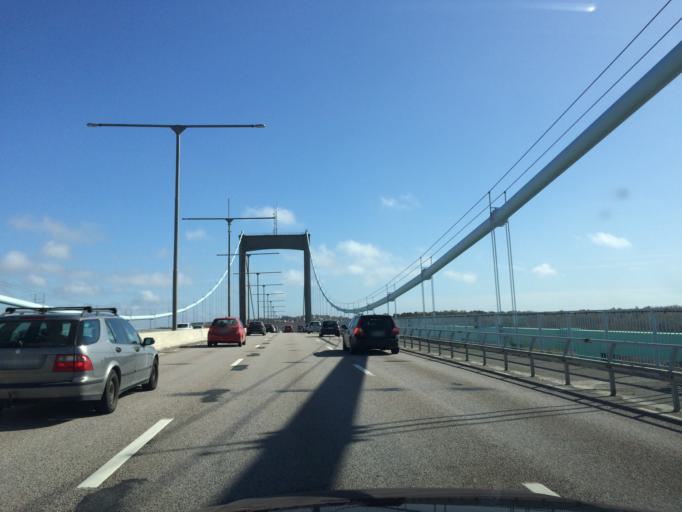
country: SE
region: Vaestra Goetaland
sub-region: Goteborg
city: Majorna
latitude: 57.6914
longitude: 11.9012
